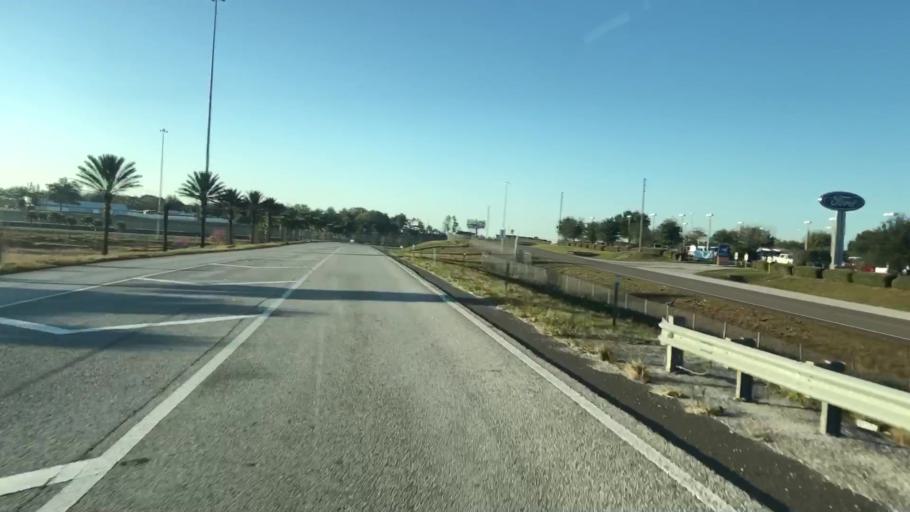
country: US
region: Florida
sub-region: Polk County
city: Loughman
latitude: 28.2330
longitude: -81.6541
